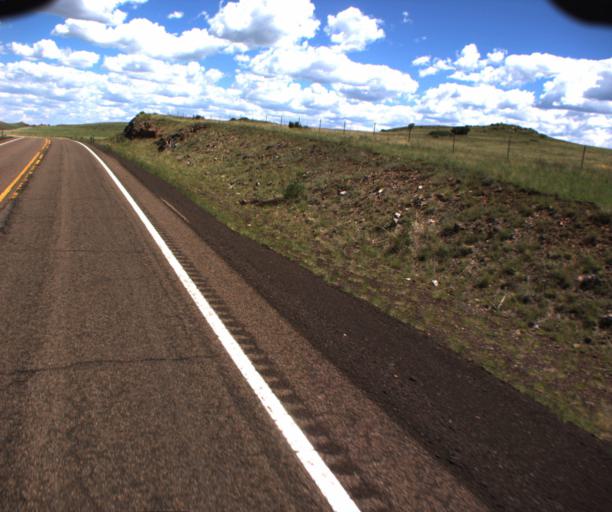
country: US
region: Arizona
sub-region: Apache County
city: Springerville
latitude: 34.2133
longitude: -109.4507
